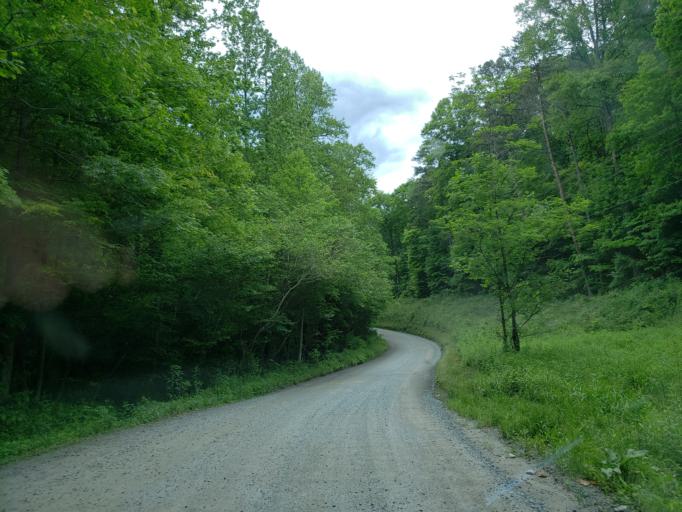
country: US
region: Georgia
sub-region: Fannin County
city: Blue Ridge
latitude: 34.8407
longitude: -84.4146
